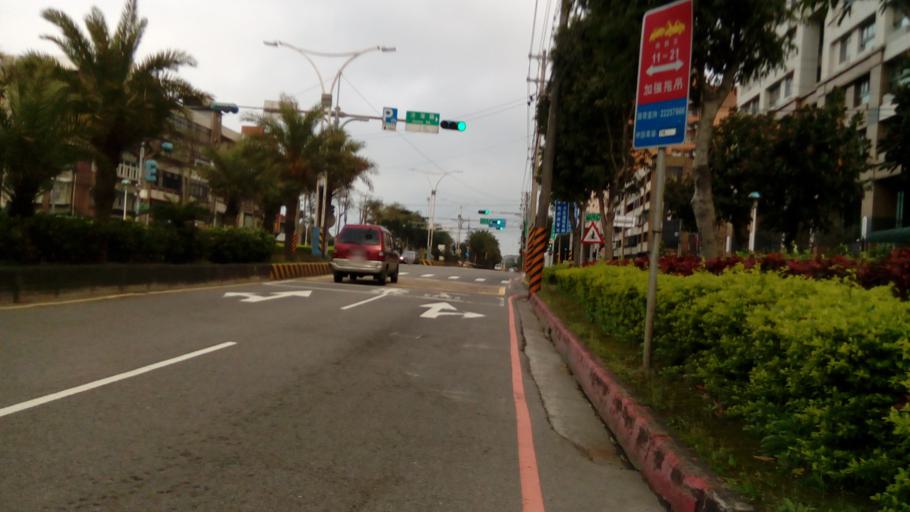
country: TW
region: Taipei
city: Taipei
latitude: 25.1772
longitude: 121.4252
